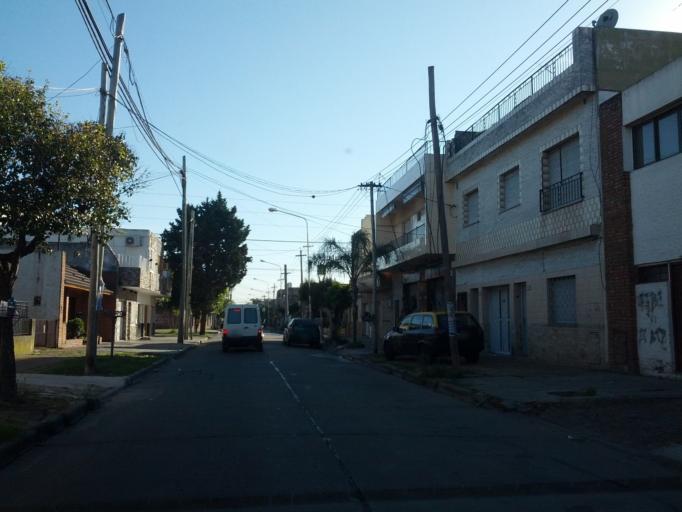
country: AR
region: Buenos Aires
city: San Justo
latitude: -34.6640
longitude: -58.5369
